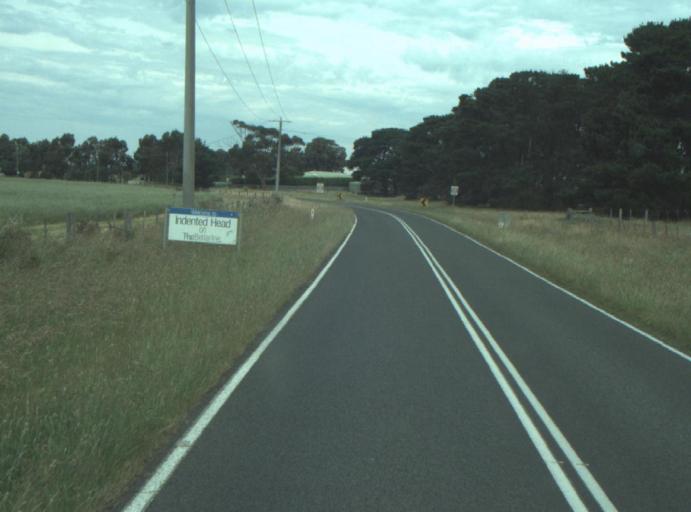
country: AU
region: Victoria
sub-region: Greater Geelong
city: Clifton Springs
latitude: -38.1281
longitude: 144.6931
